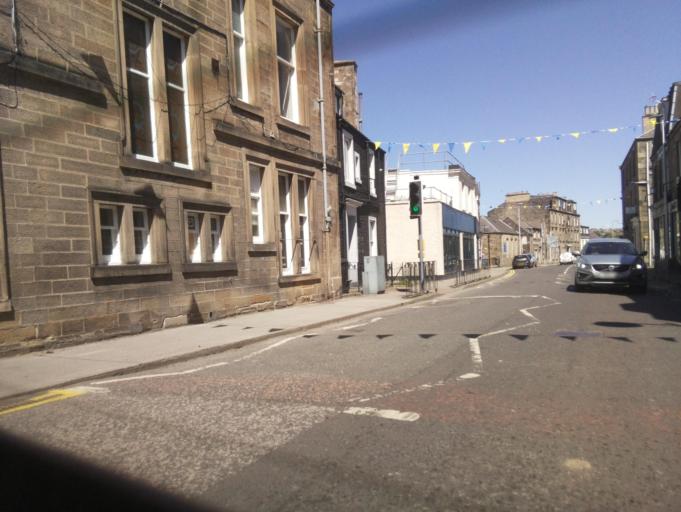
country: GB
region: Scotland
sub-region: The Scottish Borders
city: Hawick
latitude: 55.4247
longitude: -2.7844
